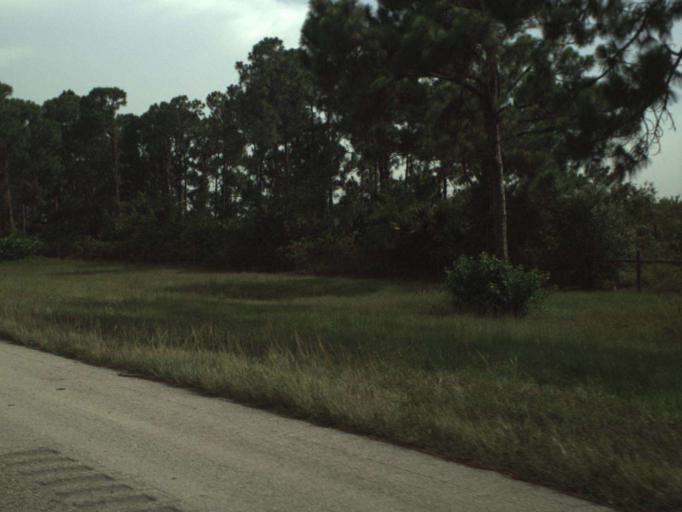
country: US
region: Florida
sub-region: Saint Lucie County
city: Port Saint Lucie
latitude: 27.2226
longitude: -80.4017
